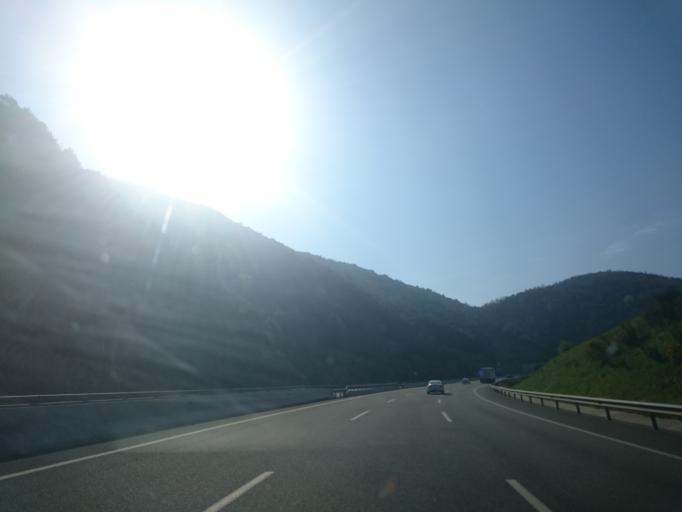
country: ES
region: Catalonia
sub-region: Provincia de Girona
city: Viladrau
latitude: 41.8865
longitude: 2.3886
